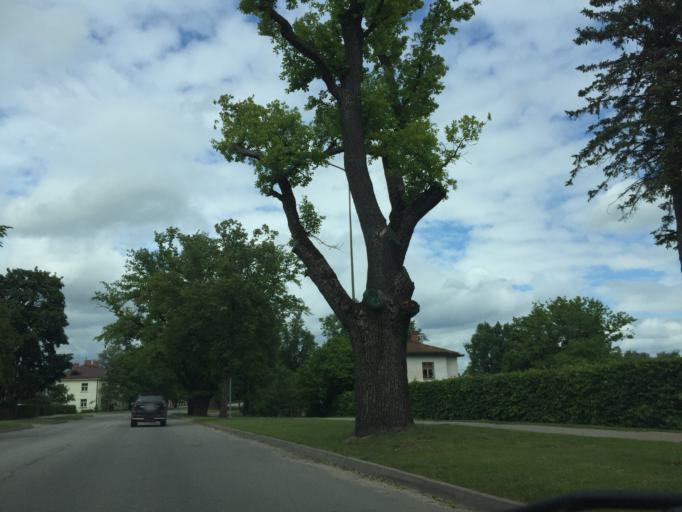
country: LV
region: Valmieras Rajons
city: Valmiera
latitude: 57.5453
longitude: 25.4313
